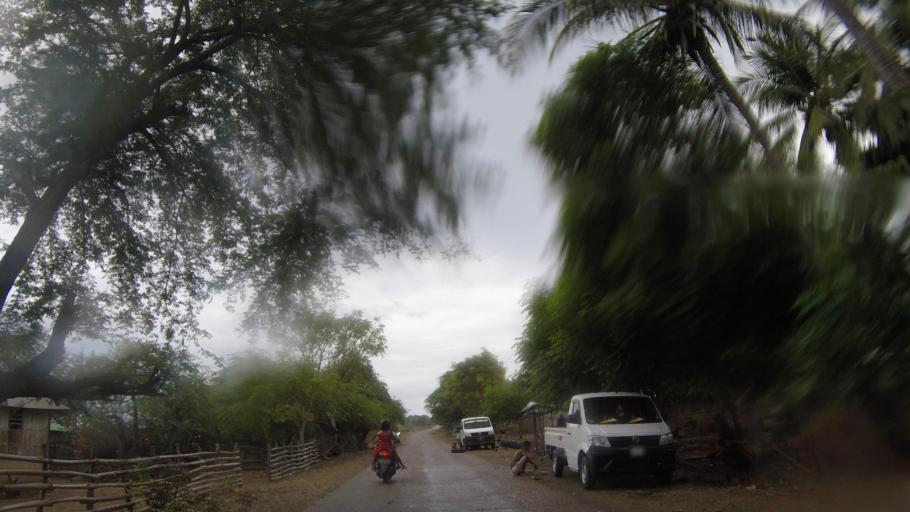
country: TL
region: Lautem
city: Lospalos
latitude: -8.3548
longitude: 126.9135
